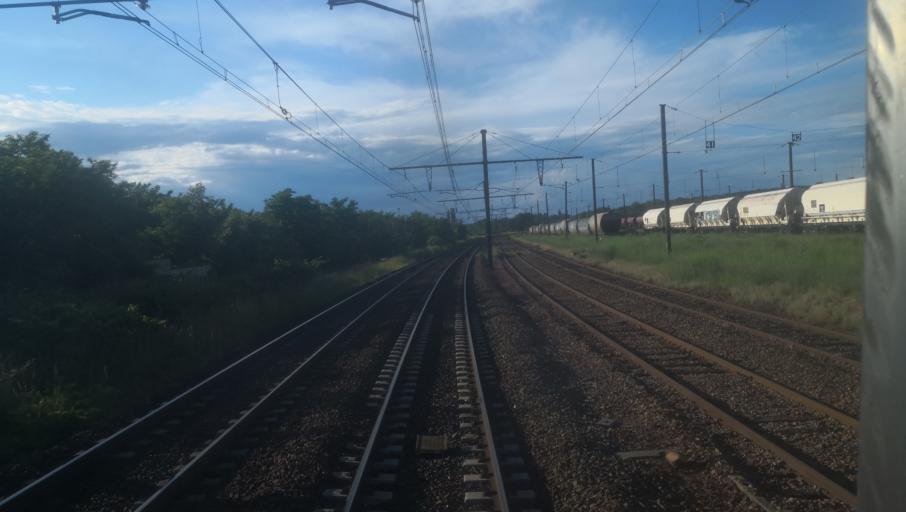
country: FR
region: Centre
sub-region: Departement du Cher
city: Vierzon
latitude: 47.2365
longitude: 2.0477
